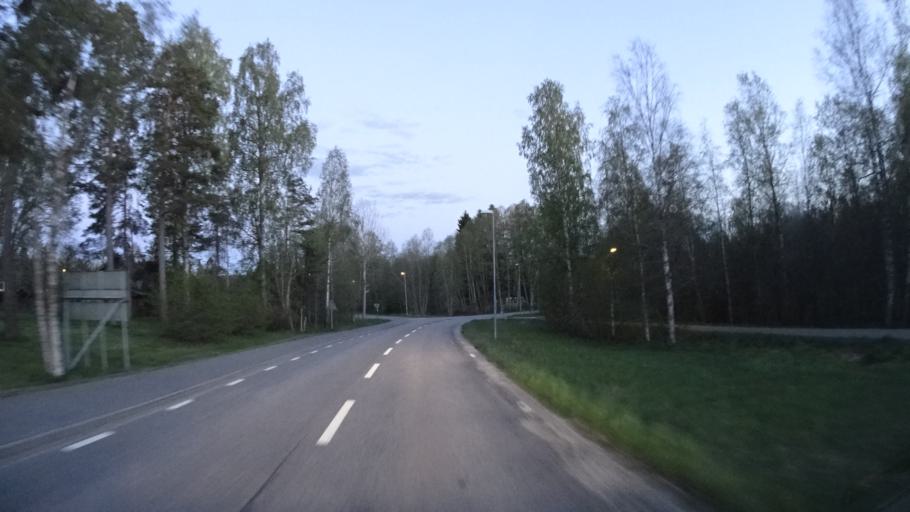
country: SE
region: OErebro
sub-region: Nora Kommun
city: As
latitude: 59.5042
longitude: 14.9641
